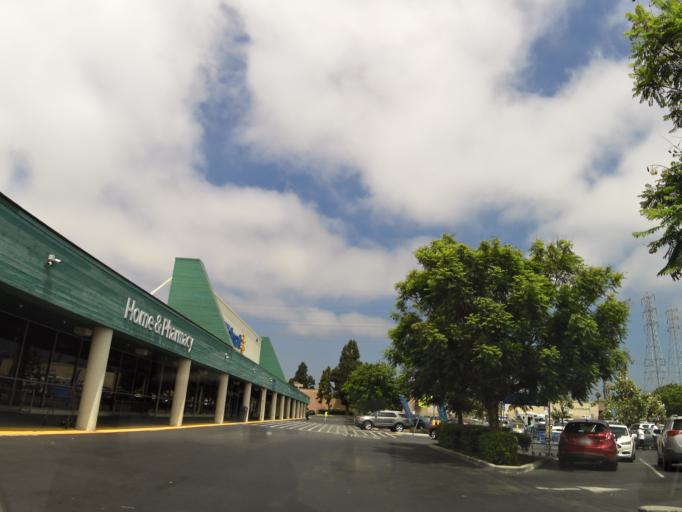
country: US
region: California
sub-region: Ventura County
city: El Rio
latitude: 34.2578
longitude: -119.2124
